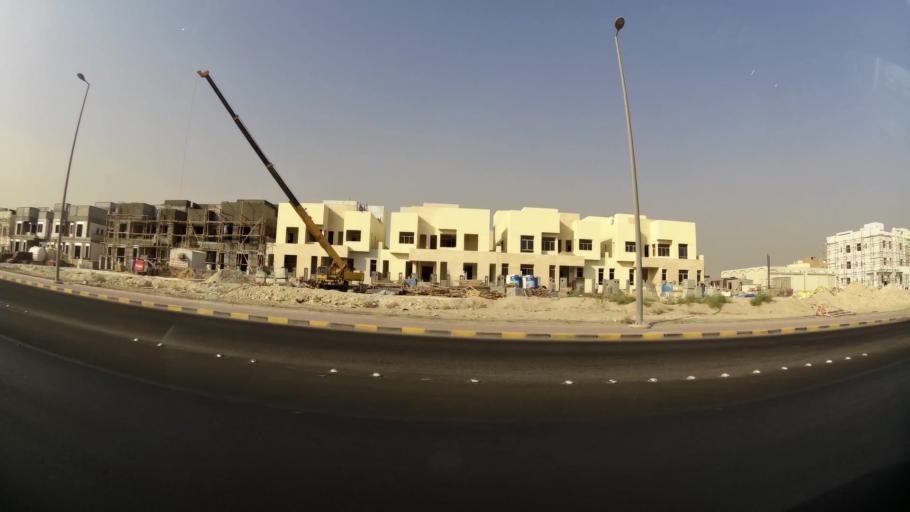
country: KW
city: Al Funaytis
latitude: 29.2240
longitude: 48.0997
